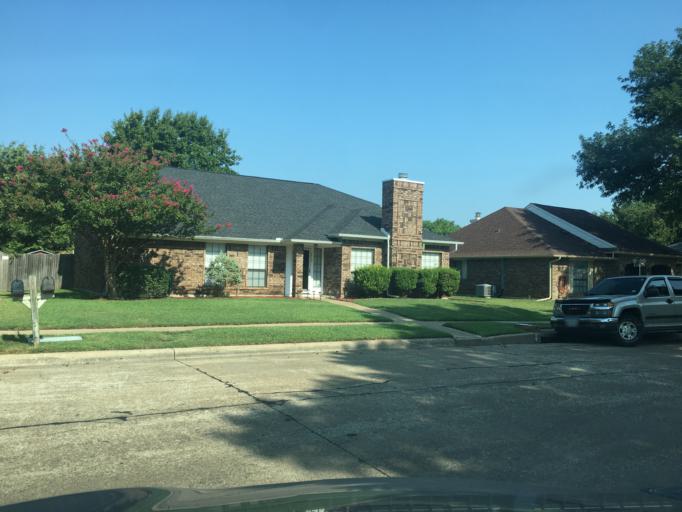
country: US
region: Texas
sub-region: Dallas County
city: Garland
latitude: 32.9453
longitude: -96.6249
